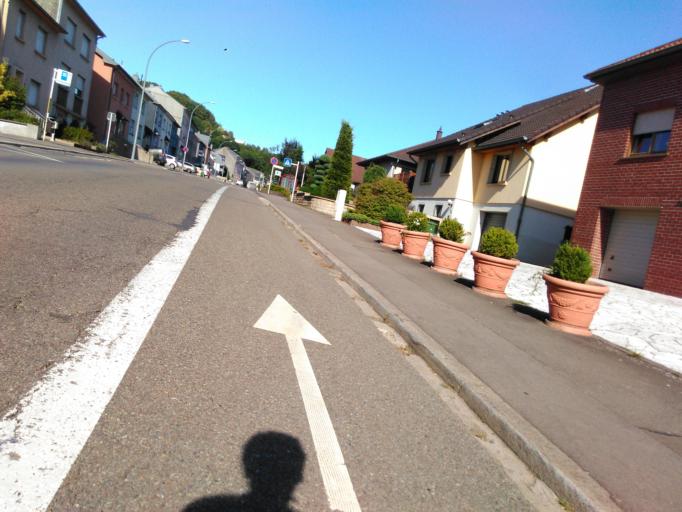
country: LU
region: Luxembourg
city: Belvaux
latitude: 49.5234
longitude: 5.9253
